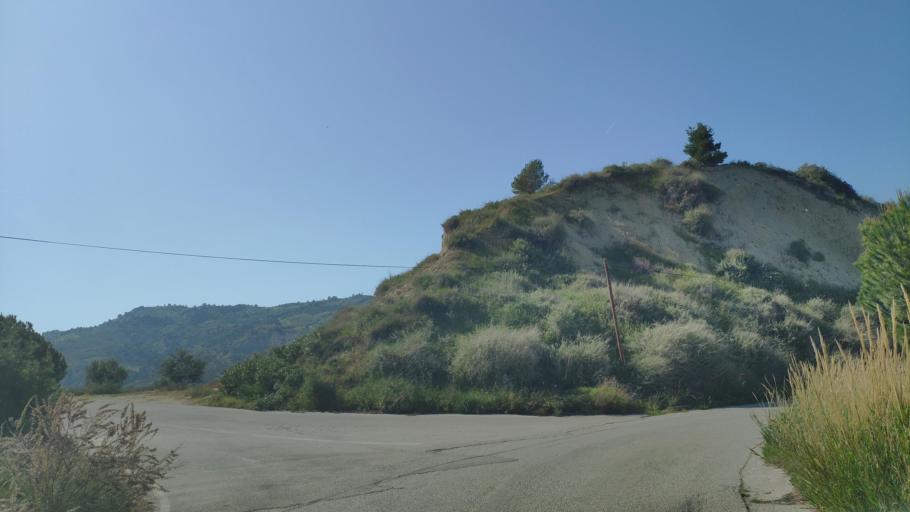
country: GR
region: West Greece
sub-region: Nomos Achaias
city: Aiyira
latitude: 38.1267
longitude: 22.3453
